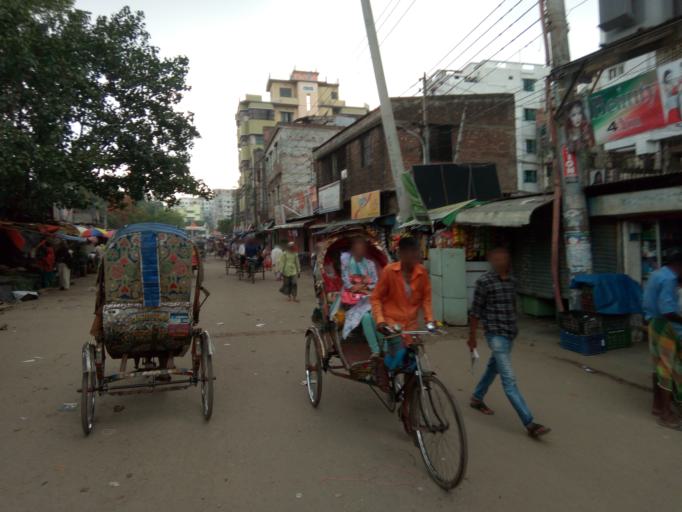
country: BD
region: Dhaka
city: Paltan
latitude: 23.7227
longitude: 90.4340
